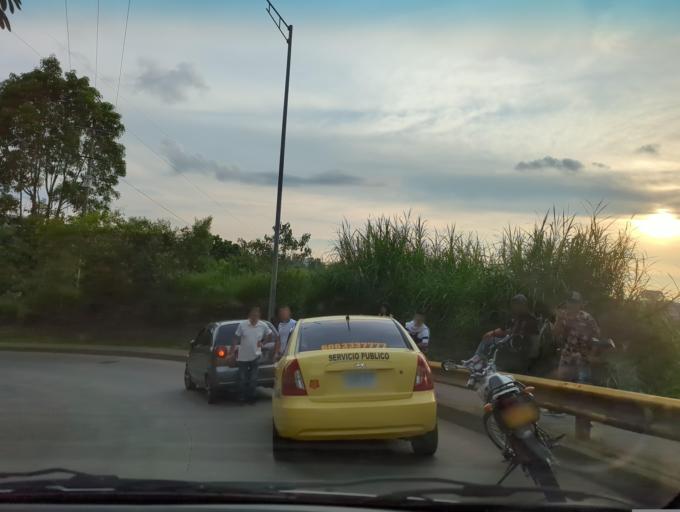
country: CO
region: Risaralda
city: Pereira
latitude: 4.8202
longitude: -75.7243
